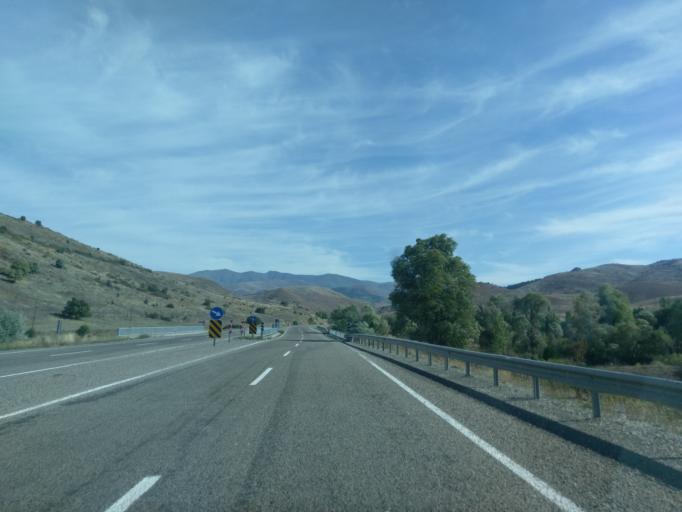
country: TR
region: Sivas
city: Imranli
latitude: 39.8408
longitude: 38.2841
